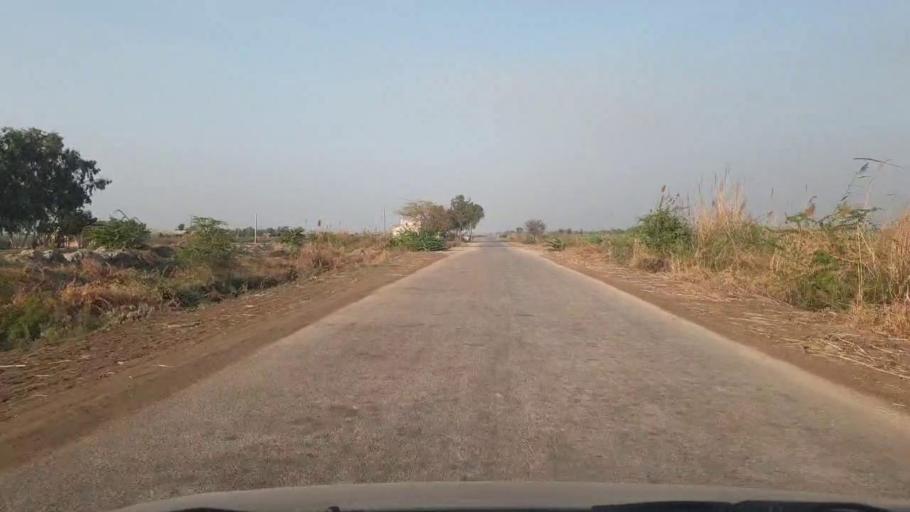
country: PK
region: Sindh
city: Mirwah Gorchani
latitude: 25.3472
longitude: 69.1715
